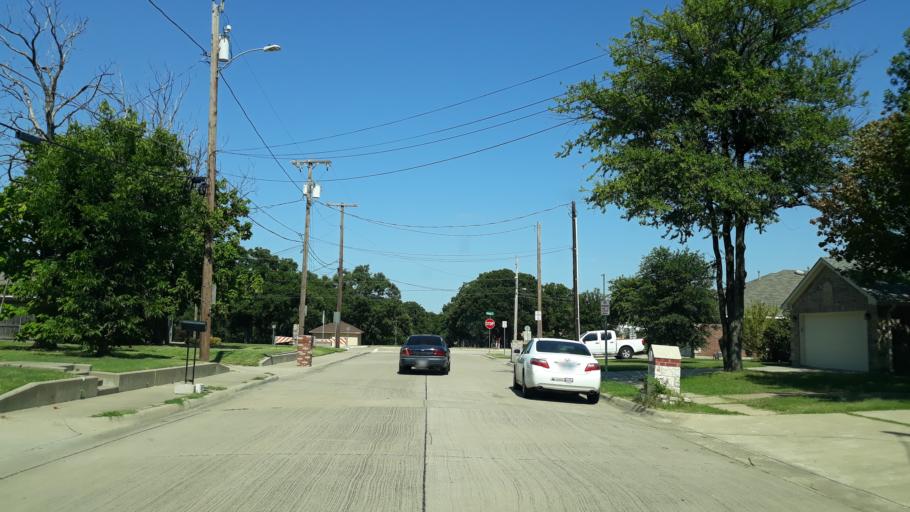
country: US
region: Texas
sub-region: Dallas County
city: Irving
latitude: 32.8191
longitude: -97.0009
